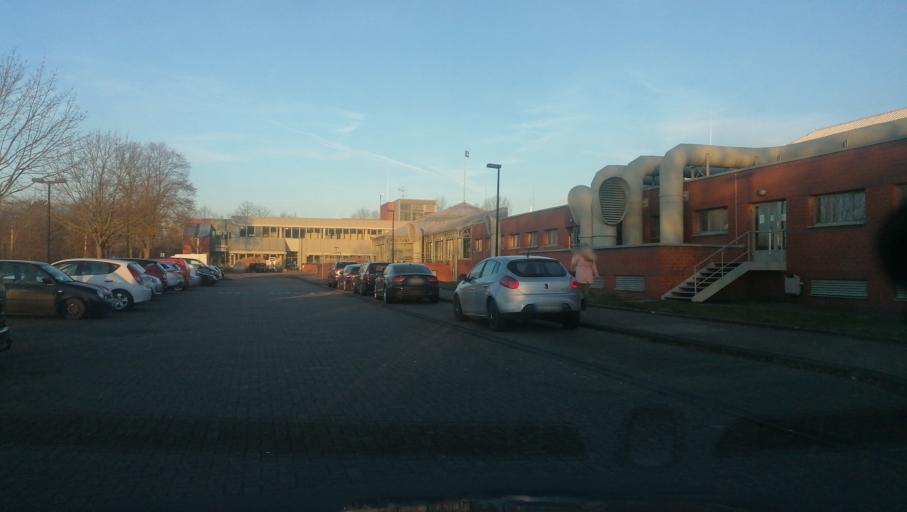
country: DE
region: North Rhine-Westphalia
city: Bergkamen
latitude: 51.6114
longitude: 7.6165
